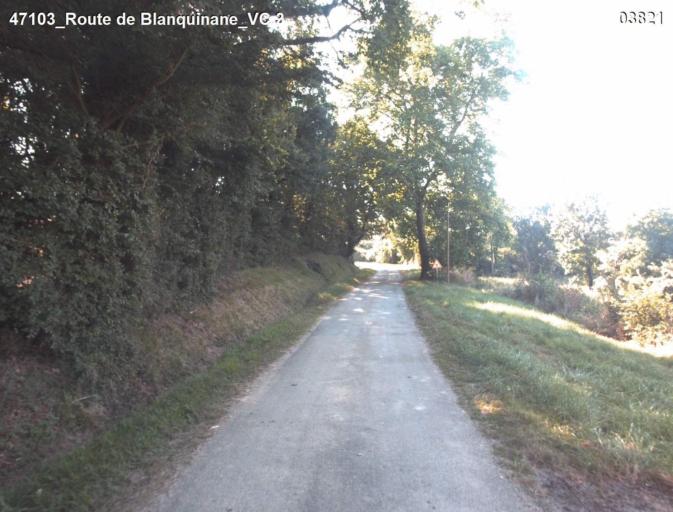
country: FR
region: Aquitaine
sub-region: Departement du Lot-et-Garonne
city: Nerac
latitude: 44.0919
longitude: 0.3211
